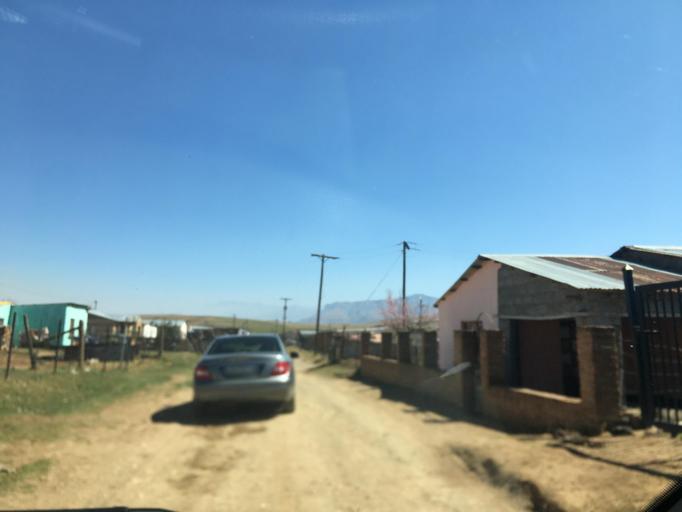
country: ZA
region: Eastern Cape
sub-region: Chris Hani District Municipality
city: Elliot
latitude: -31.3296
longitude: 27.8202
